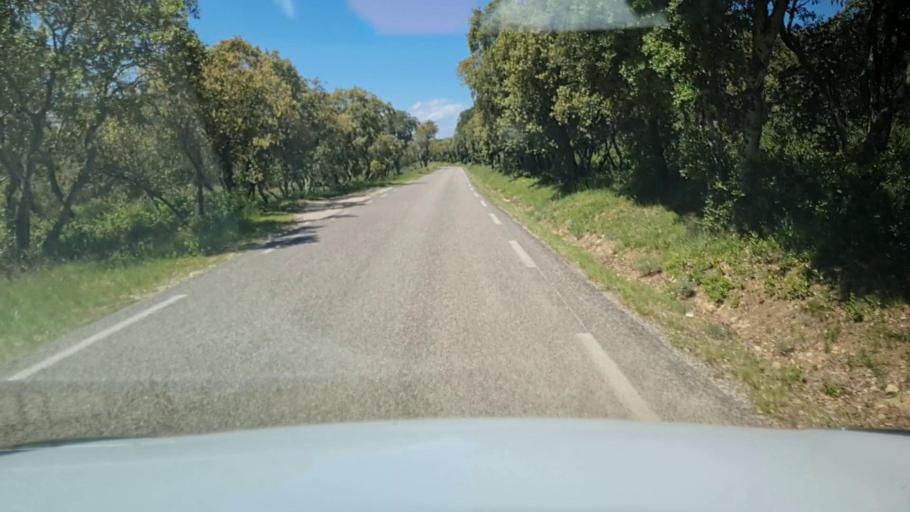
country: FR
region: Languedoc-Roussillon
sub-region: Departement du Gard
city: Clarensac
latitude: 43.8518
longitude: 4.2172
